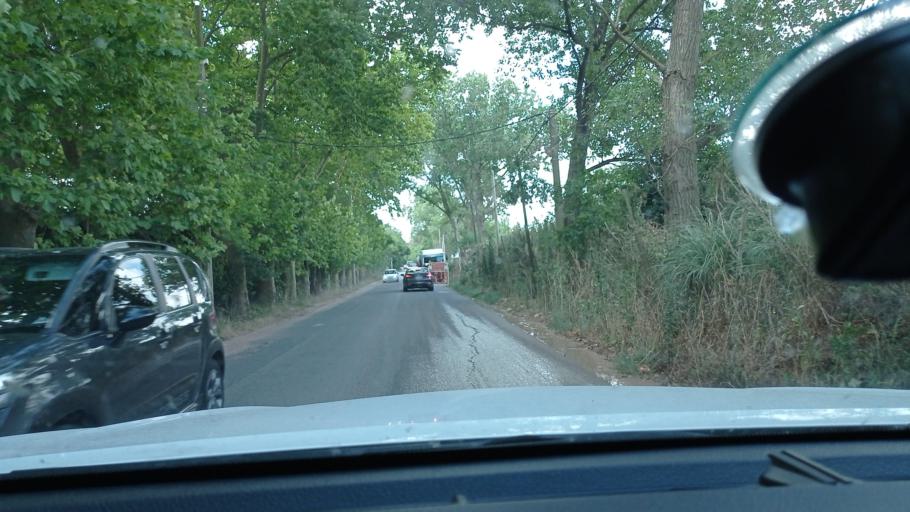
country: UY
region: Canelones
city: La Paz
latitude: -34.8138
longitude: -56.1941
